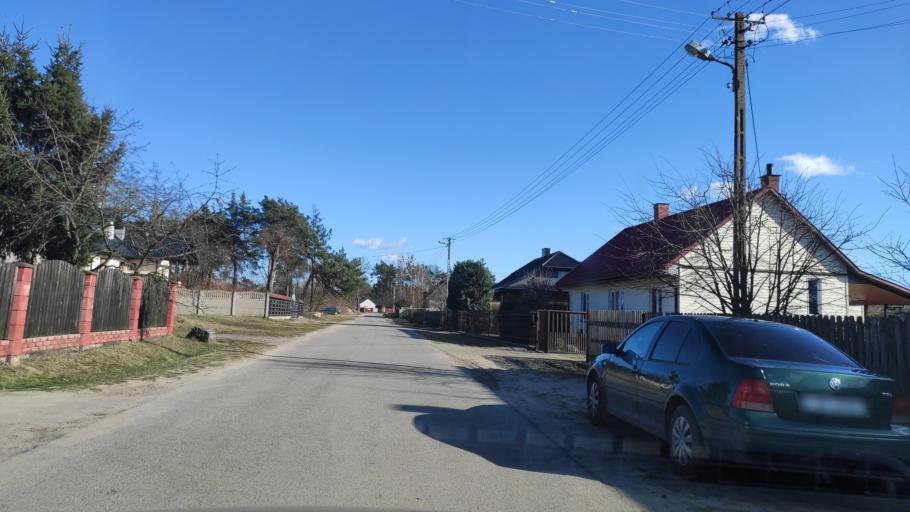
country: PL
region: Masovian Voivodeship
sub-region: Powiat radomski
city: Jastrzebia
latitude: 51.4563
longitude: 21.2698
